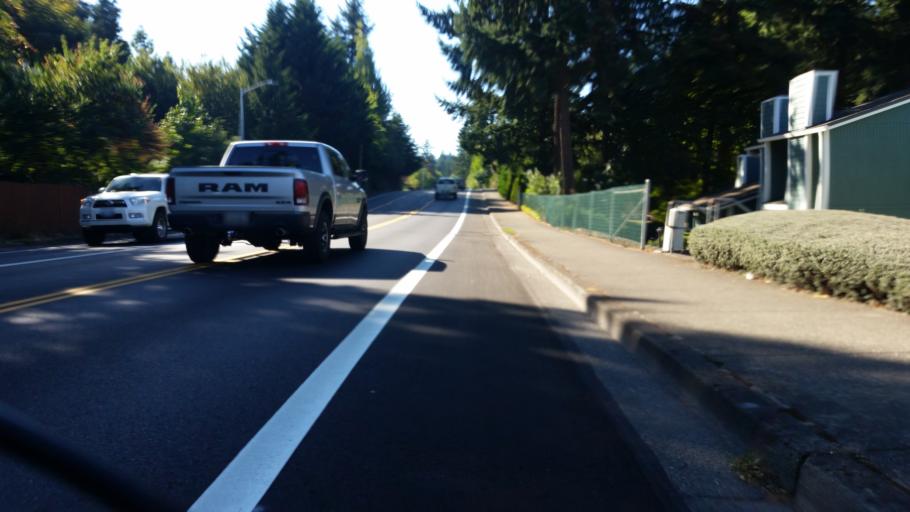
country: US
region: Oregon
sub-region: Washington County
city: Durham
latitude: 45.4152
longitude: -122.7587
